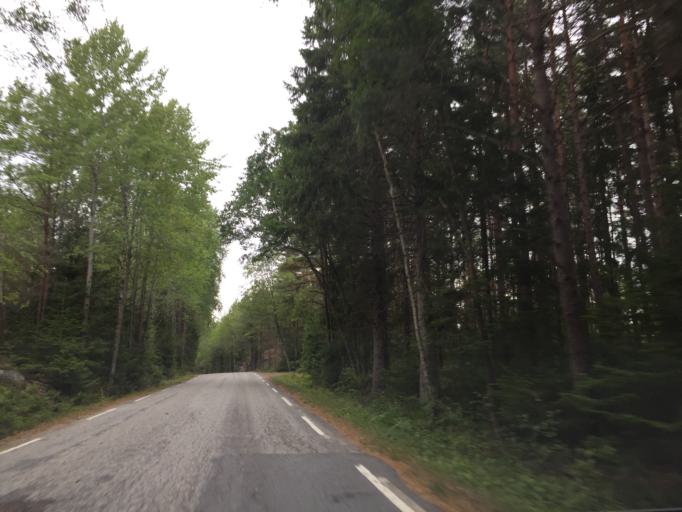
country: NO
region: Ostfold
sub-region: Hvaler
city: Skjaerhalden
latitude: 59.0747
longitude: 11.0239
